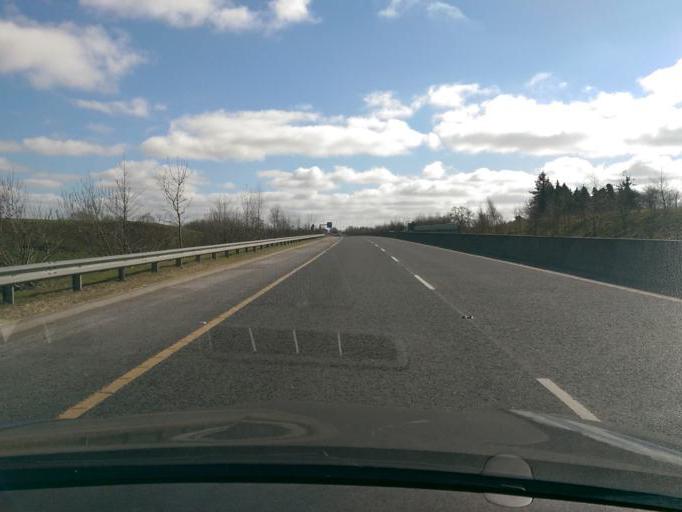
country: IE
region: Leinster
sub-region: An Iarmhi
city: Kilbeggan
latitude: 53.3603
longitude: -7.5121
